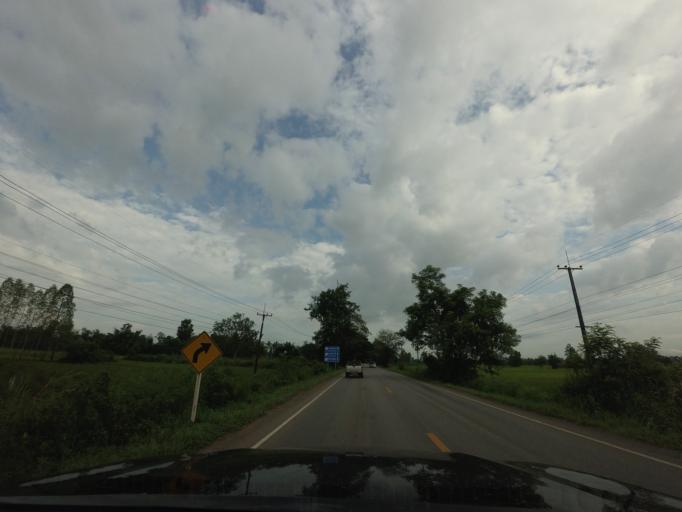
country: TH
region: Changwat Udon Thani
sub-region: Amphoe Ban Phue
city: Ban Phue
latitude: 17.7537
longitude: 102.3983
